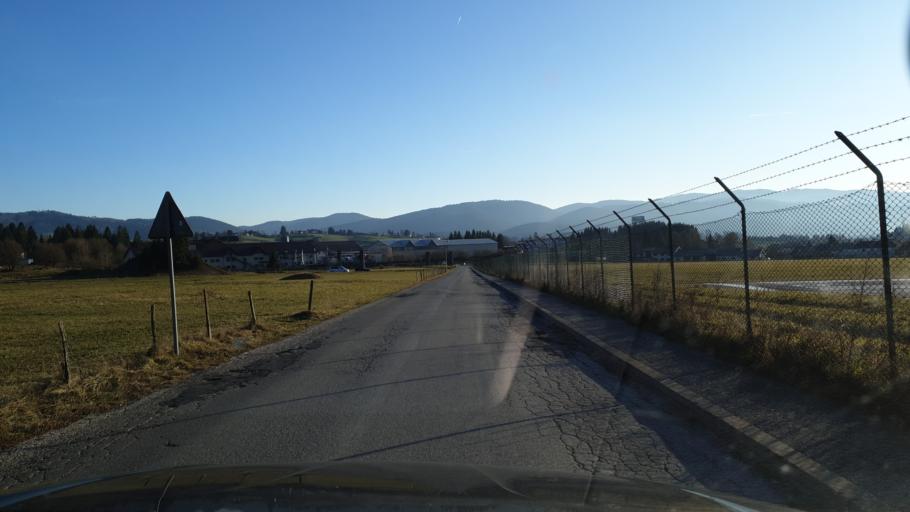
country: IT
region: Veneto
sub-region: Provincia di Vicenza
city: Gallio
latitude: 45.8883
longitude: 11.5227
